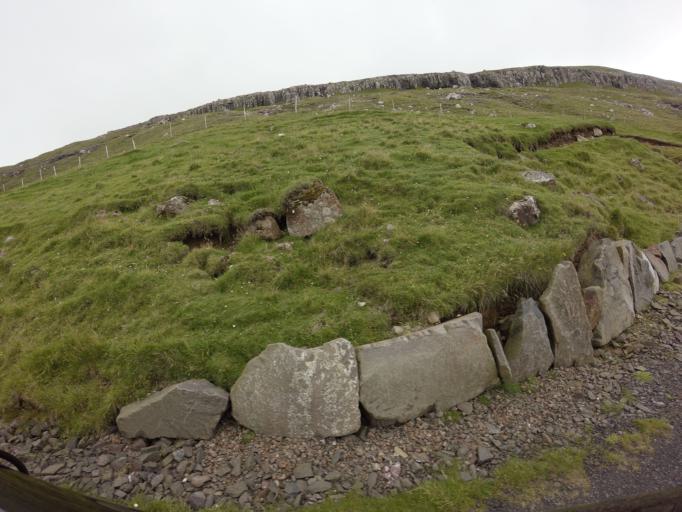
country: FO
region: Sandoy
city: Sandur
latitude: 61.8093
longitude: -6.7520
